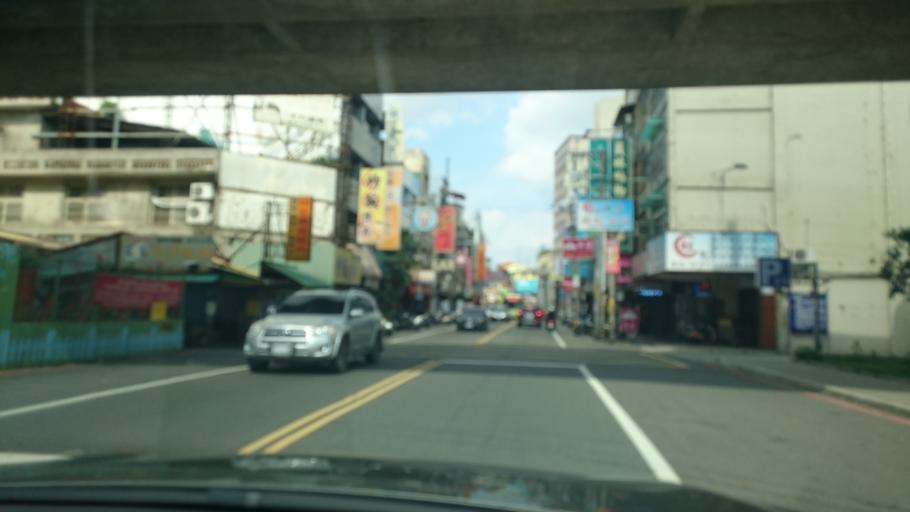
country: TW
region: Taiwan
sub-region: Nantou
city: Nantou
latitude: 23.9623
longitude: 120.5696
